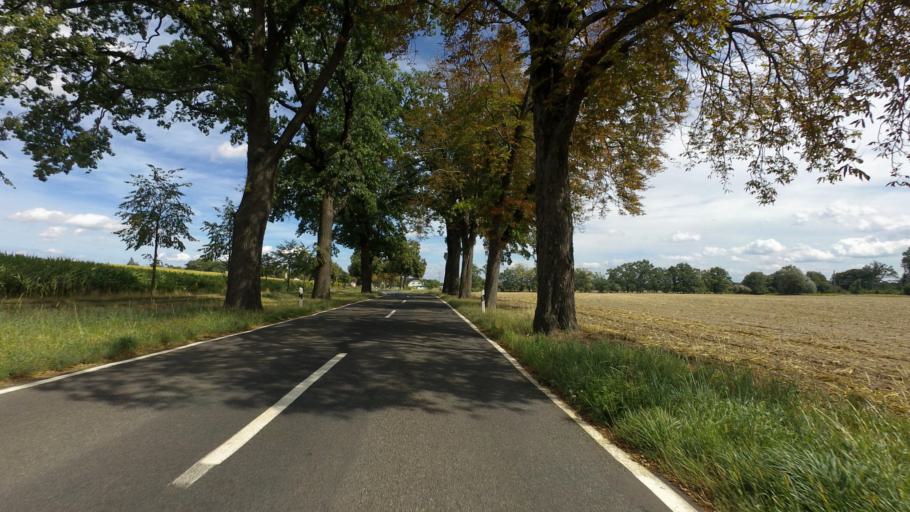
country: DE
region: Brandenburg
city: Gross Kreutz
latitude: 52.4128
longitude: 12.7839
